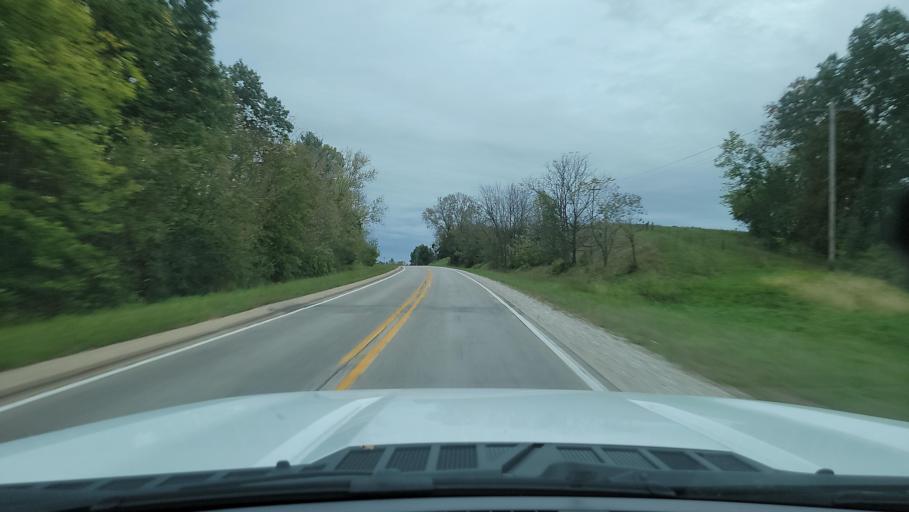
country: US
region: Illinois
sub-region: Schuyler County
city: Rushville
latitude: 40.0385
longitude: -90.6170
